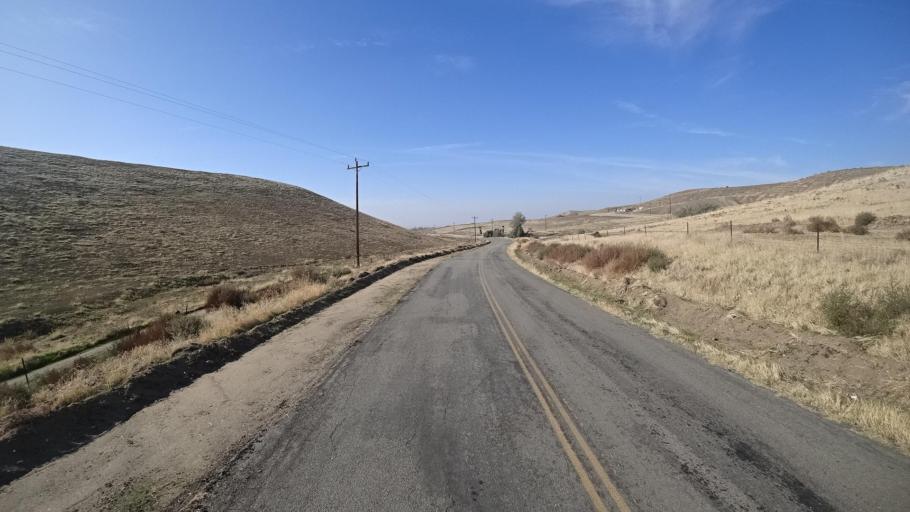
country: US
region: California
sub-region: Kern County
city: Lamont
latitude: 35.3867
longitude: -118.8197
